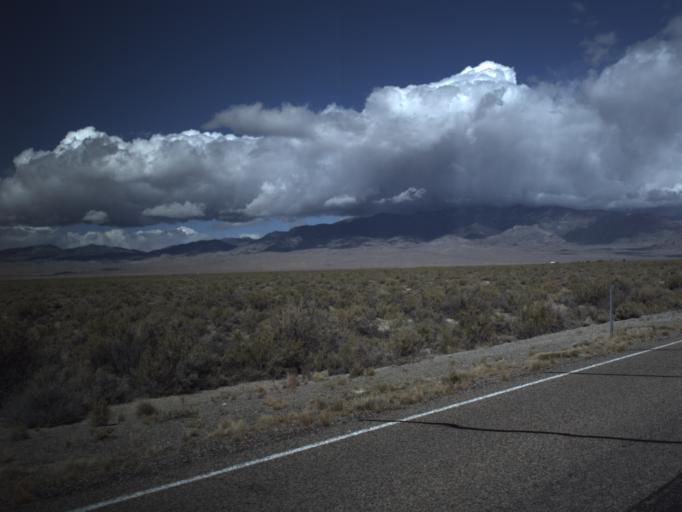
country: US
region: Nevada
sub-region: White Pine County
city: McGill
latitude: 39.0307
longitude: -114.0357
